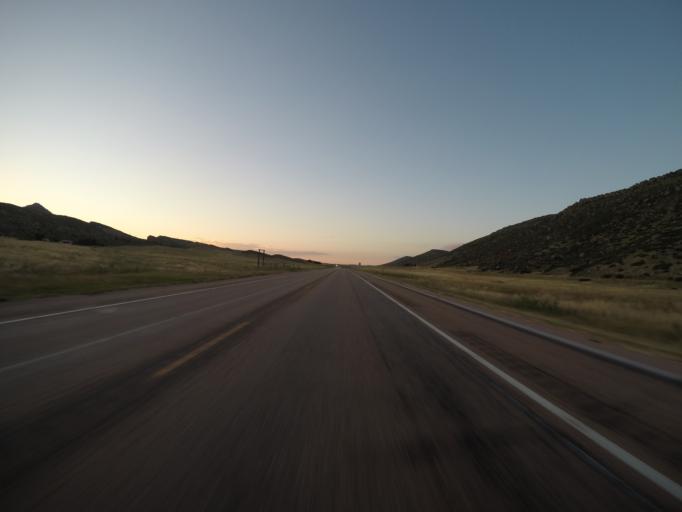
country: US
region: Colorado
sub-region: Larimer County
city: Laporte
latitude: 40.7203
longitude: -105.1719
